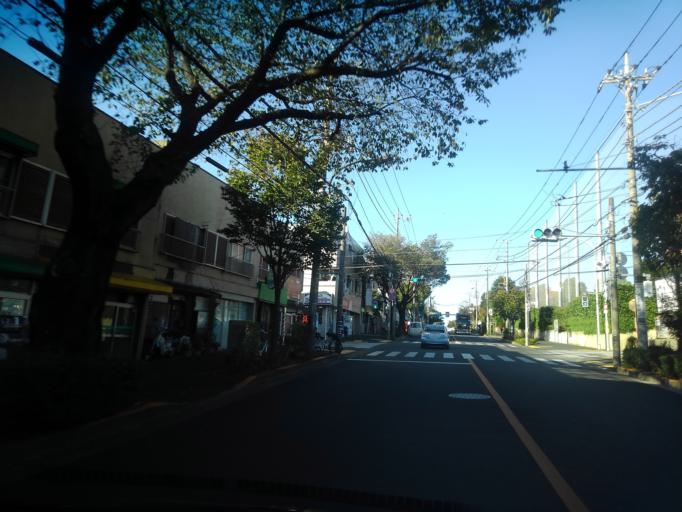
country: JP
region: Tokyo
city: Kokubunji
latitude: 35.7094
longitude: 139.4962
